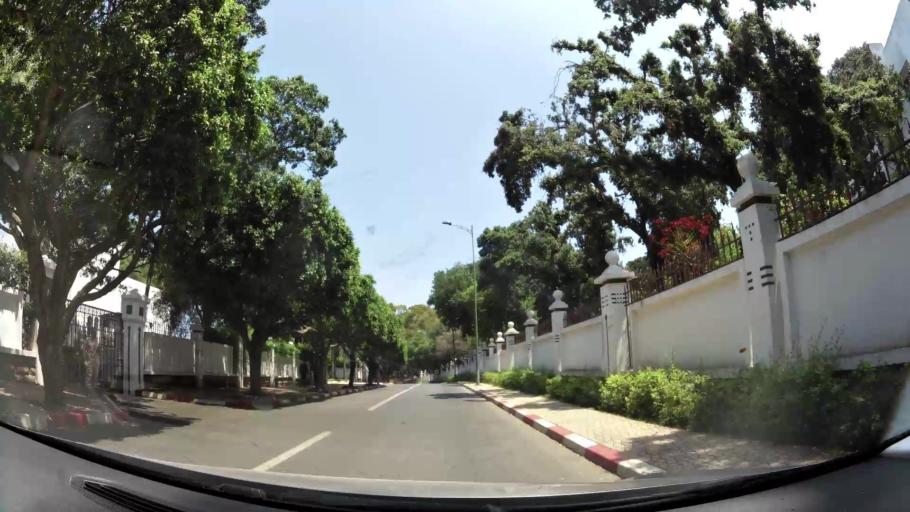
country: MA
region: Rabat-Sale-Zemmour-Zaer
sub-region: Rabat
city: Rabat
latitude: 34.0100
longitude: -6.8263
